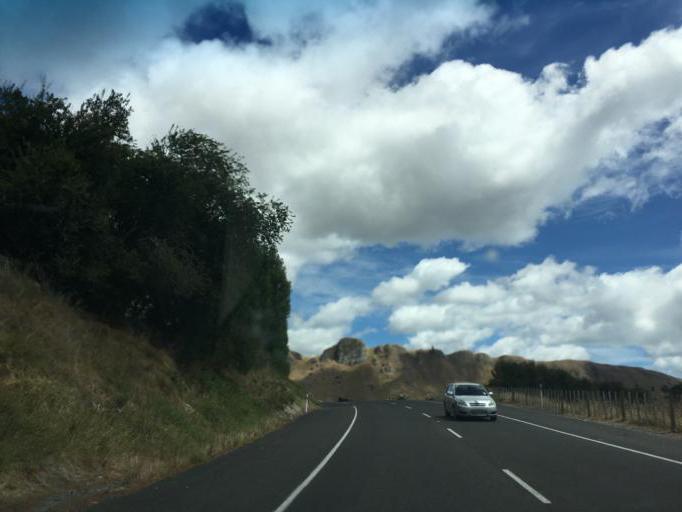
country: NZ
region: Hawke's Bay
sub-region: Hastings District
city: Hastings
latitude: -39.7009
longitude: 176.9293
